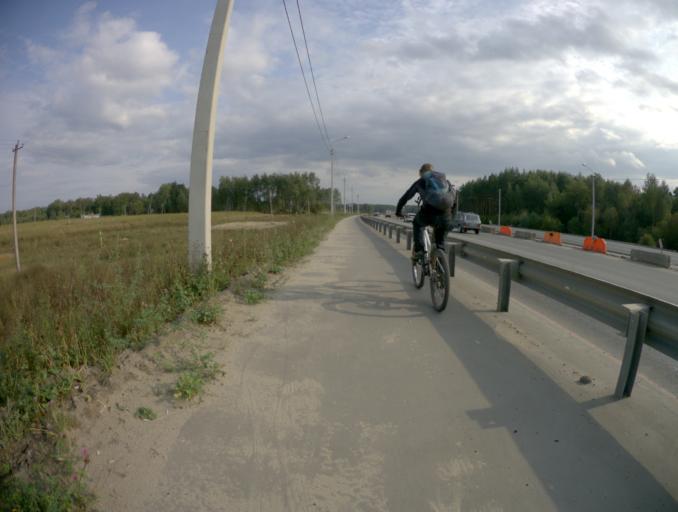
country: RU
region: Vladimir
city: Kommunar
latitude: 56.0692
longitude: 40.4981
